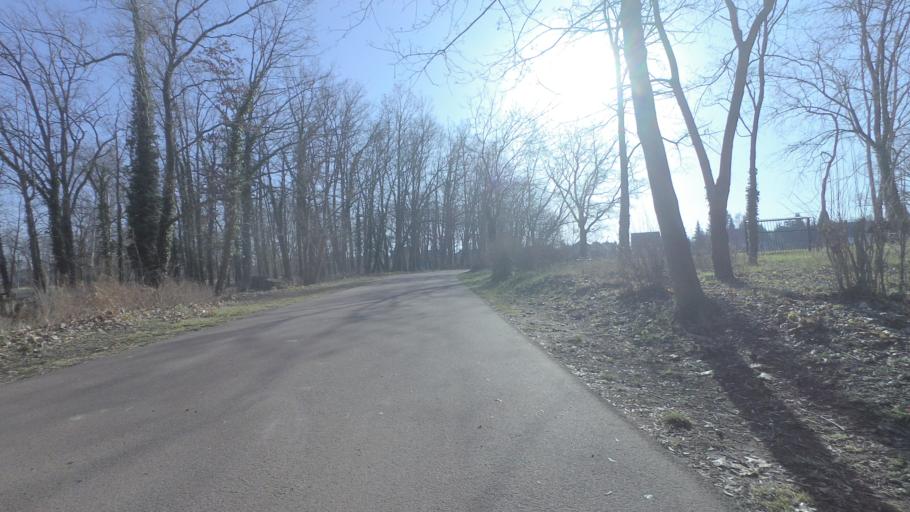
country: DE
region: Brandenburg
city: Luckenwalde
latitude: 52.0818
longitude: 13.1736
